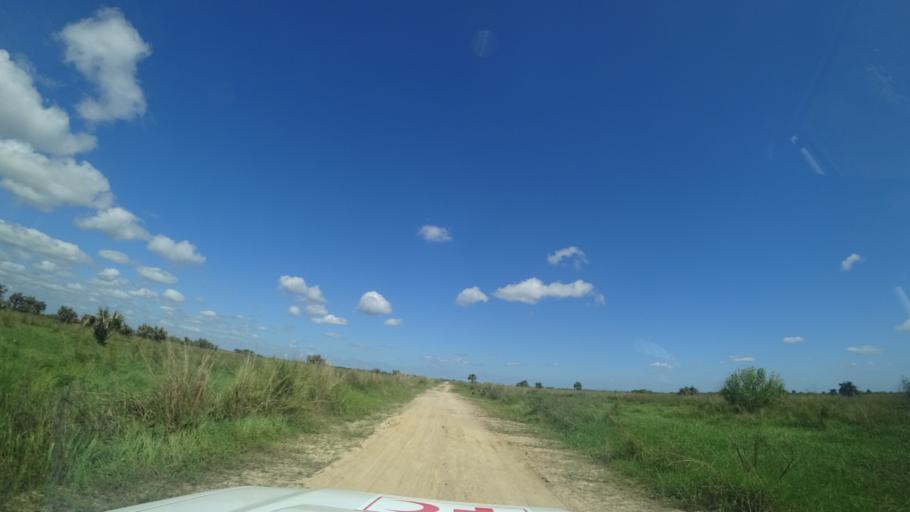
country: MZ
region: Sofala
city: Dondo
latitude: -19.3905
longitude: 34.5773
